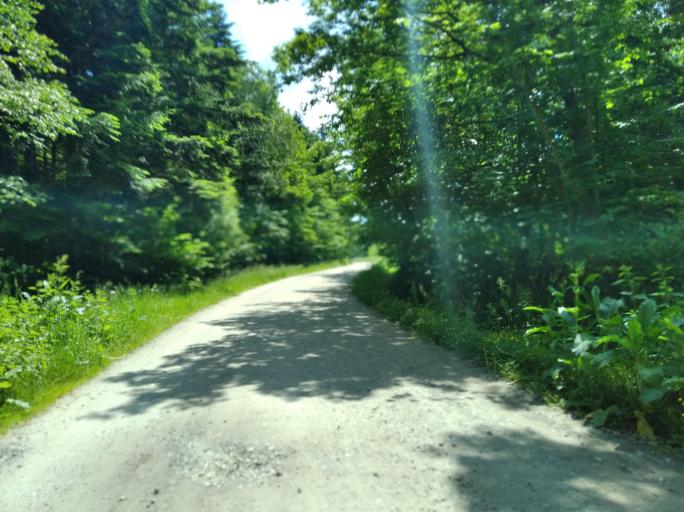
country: PL
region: Subcarpathian Voivodeship
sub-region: Powiat ropczycko-sedziszowski
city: Zagorzyce
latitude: 49.9724
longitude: 21.6868
